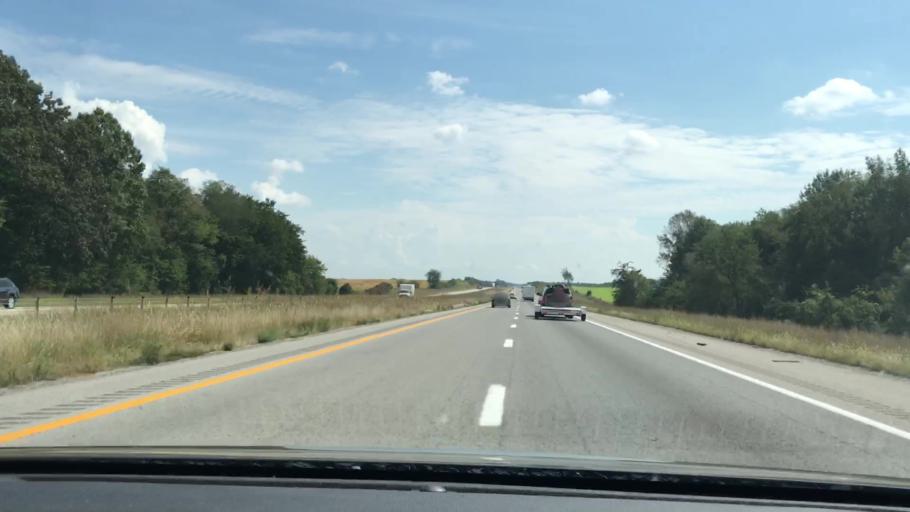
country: US
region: Kentucky
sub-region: Christian County
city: Hopkinsville
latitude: 36.7748
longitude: -87.5637
